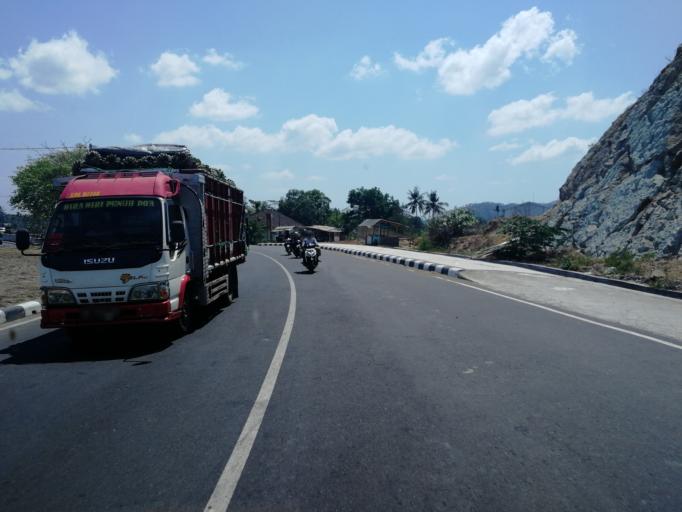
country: ID
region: West Nusa Tenggara
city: Jelateng Timur
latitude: -8.6917
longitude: 116.1117
